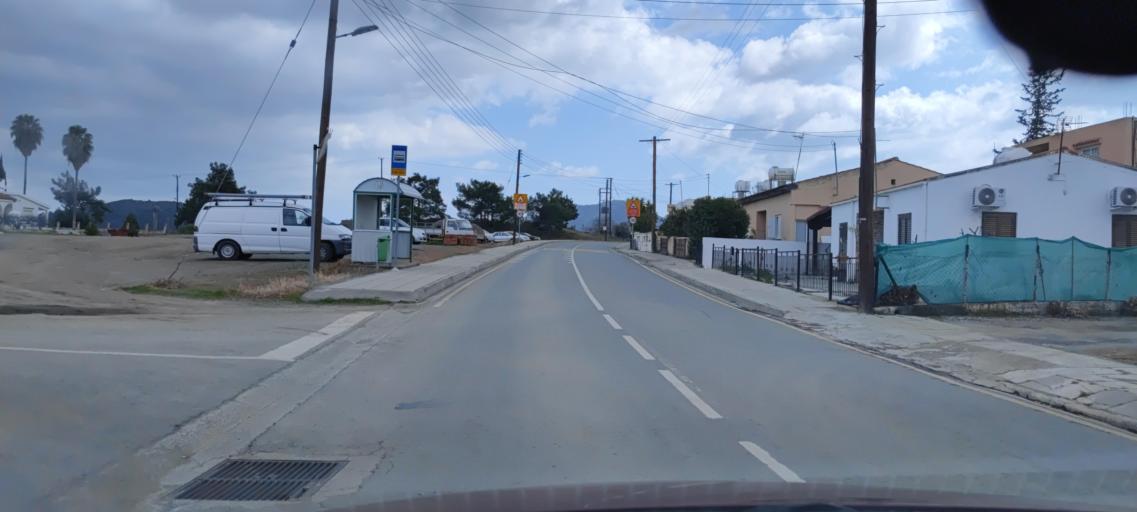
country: CY
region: Larnaka
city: Kornos
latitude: 34.9179
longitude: 33.4004
